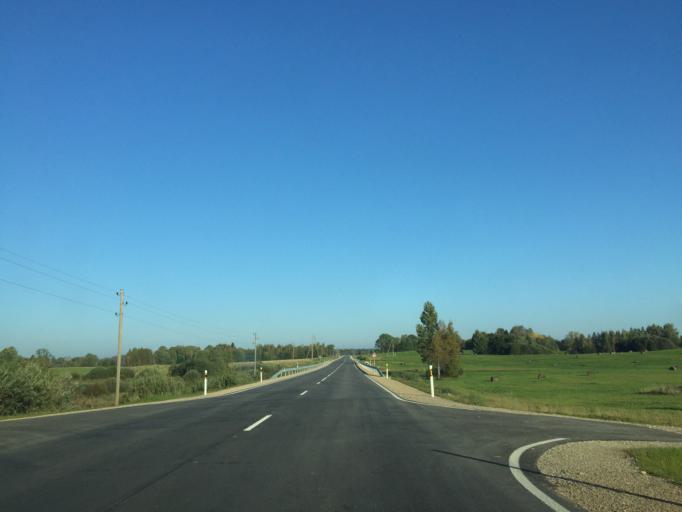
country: LV
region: Vecpiebalga
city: Vecpiebalga
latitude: 57.0868
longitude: 25.7423
